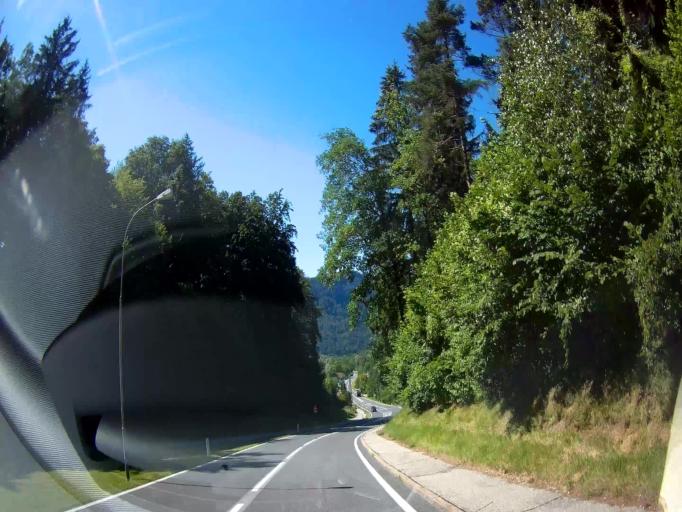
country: AT
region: Carinthia
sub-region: Politischer Bezirk Volkermarkt
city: Gallizien
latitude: 46.5603
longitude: 14.5058
